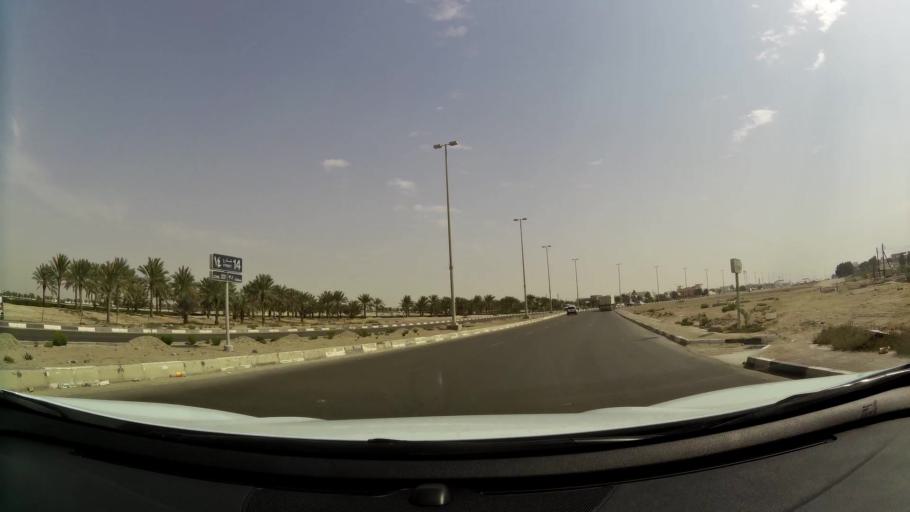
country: AE
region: Abu Dhabi
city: Abu Dhabi
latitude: 24.3043
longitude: 54.6289
